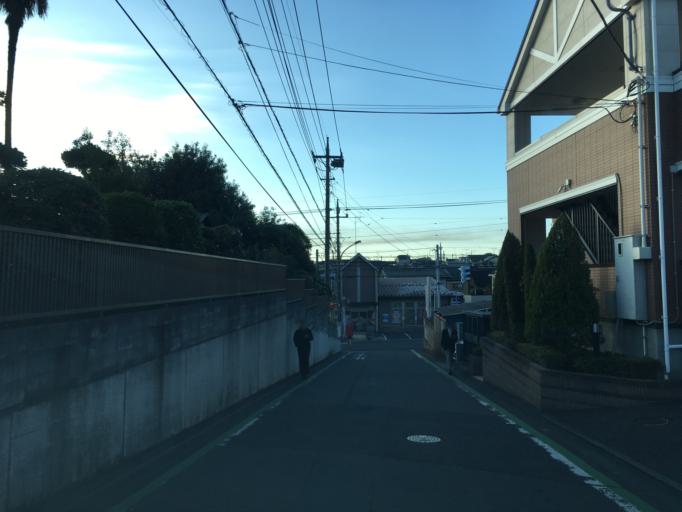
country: JP
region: Saitama
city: Tokorozawa
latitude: 35.7912
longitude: 139.4327
